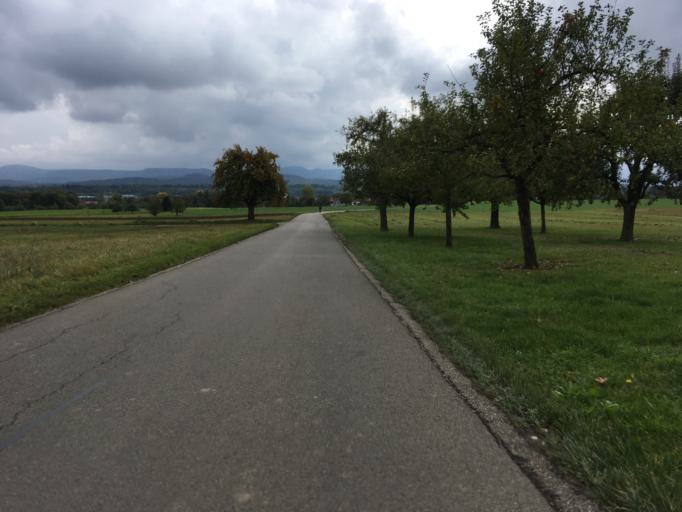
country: DE
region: Baden-Wuerttemberg
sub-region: Tuebingen Region
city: Kusterdingen
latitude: 48.5108
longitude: 9.1243
